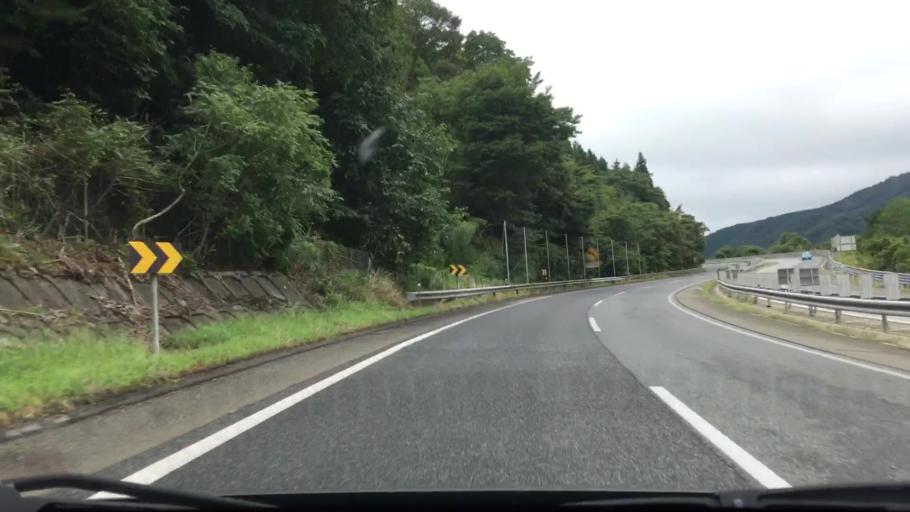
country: JP
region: Hiroshima
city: Shobara
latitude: 34.8473
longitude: 133.0915
